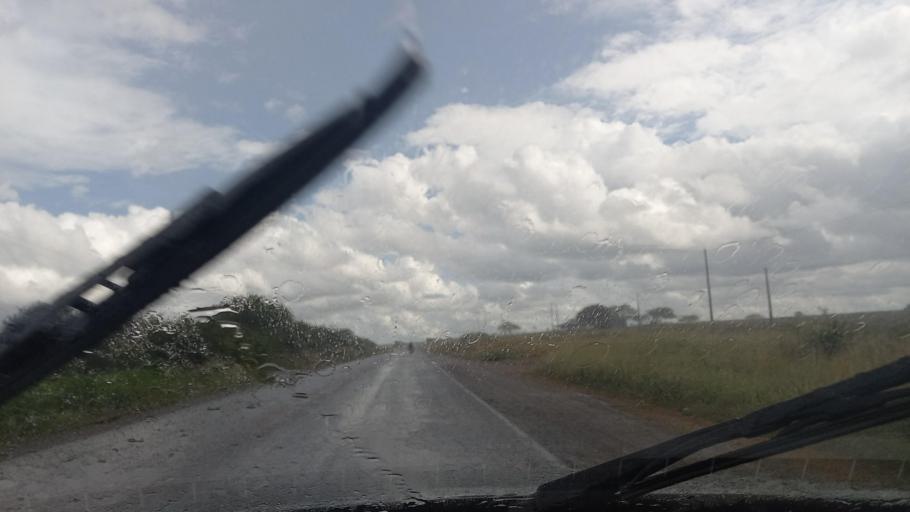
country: BR
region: Pernambuco
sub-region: Lajedo
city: Lajedo
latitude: -8.5757
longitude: -36.2851
